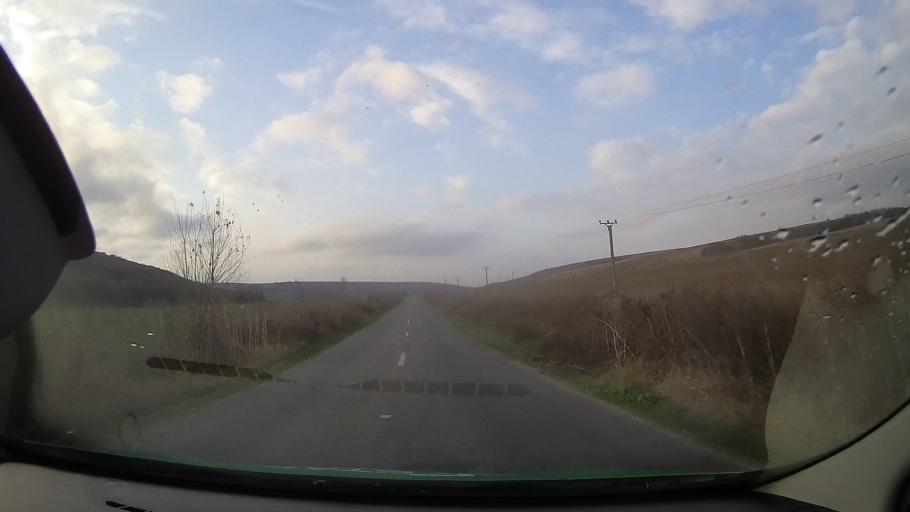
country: RO
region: Constanta
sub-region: Comuna Dobromir
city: Dobromir
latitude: 44.0320
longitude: 27.8571
